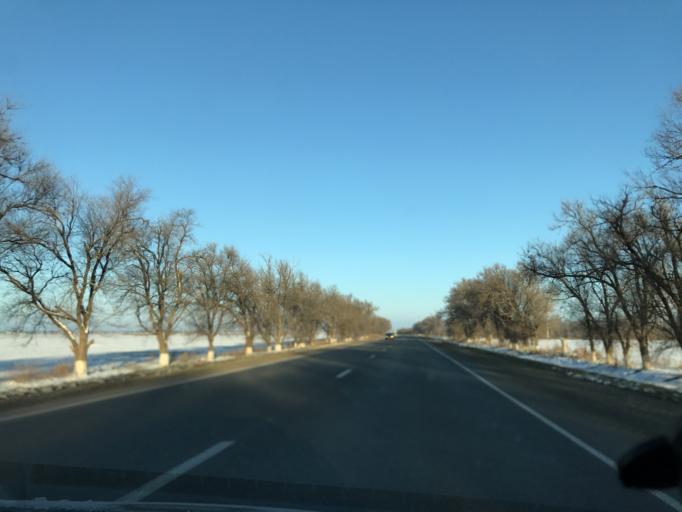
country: RU
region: Stavropol'skiy
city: Bezopasnoye
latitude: 45.6233
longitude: 41.9344
